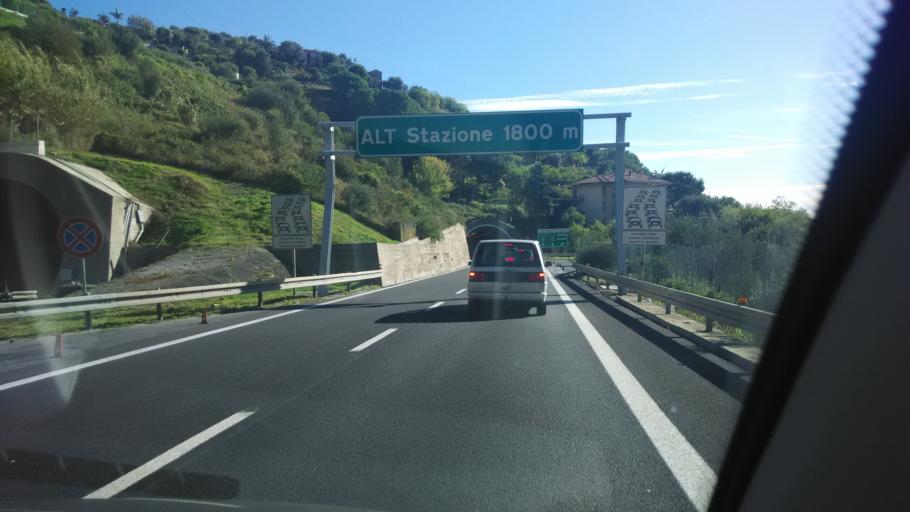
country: IT
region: Liguria
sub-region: Provincia di Imperia
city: Ventimiglia
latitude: 43.7975
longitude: 7.5708
